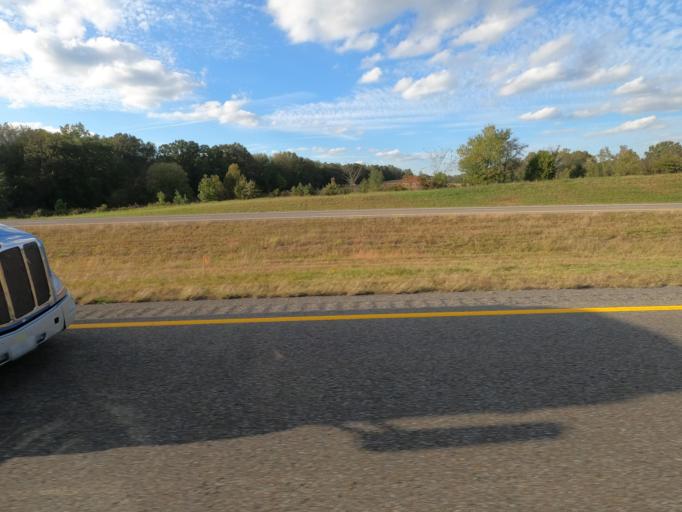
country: US
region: Tennessee
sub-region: Henderson County
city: Lexington
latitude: 35.7858
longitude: -88.4033
